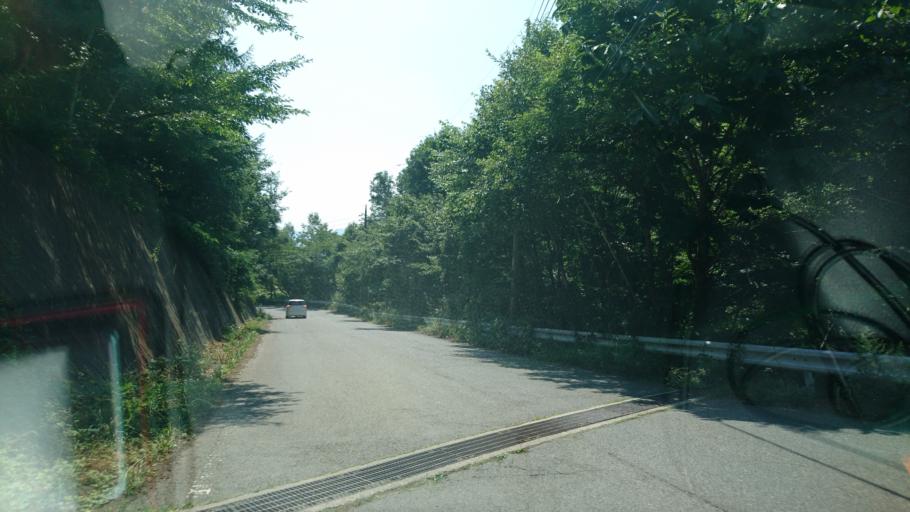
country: JP
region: Gunma
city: Numata
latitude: 36.7645
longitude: 139.2497
